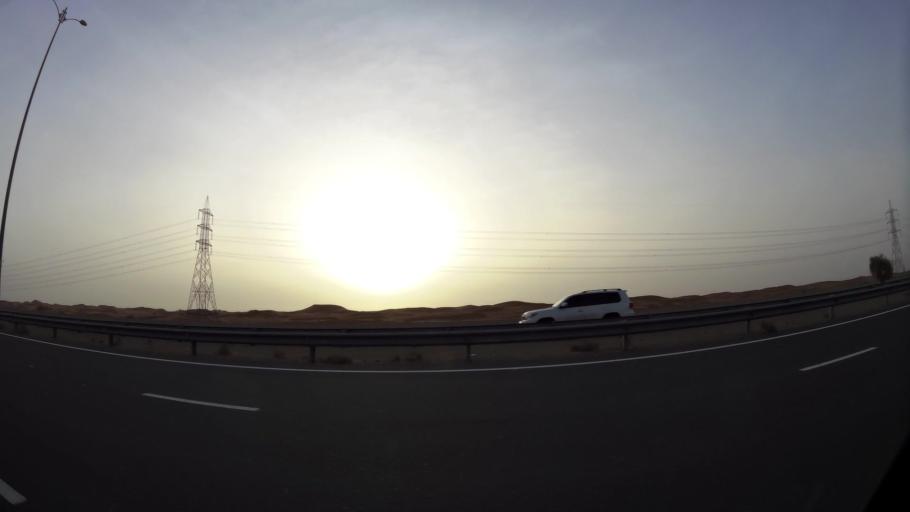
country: OM
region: Al Buraimi
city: Al Buraymi
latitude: 24.3669
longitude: 55.7926
